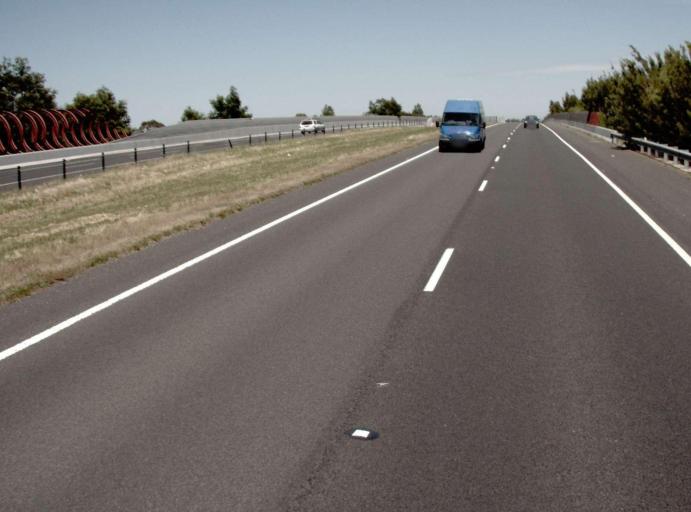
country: AU
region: Victoria
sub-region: Cardinia
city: Pakenham South
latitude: -38.0842
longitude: 145.5152
